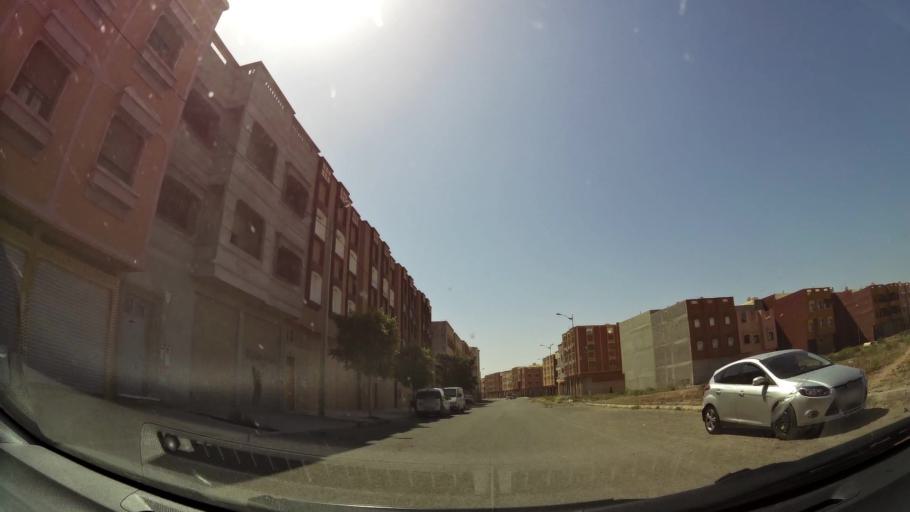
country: MA
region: Souss-Massa-Draa
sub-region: Inezgane-Ait Mellou
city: Inezgane
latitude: 30.3327
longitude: -9.5094
